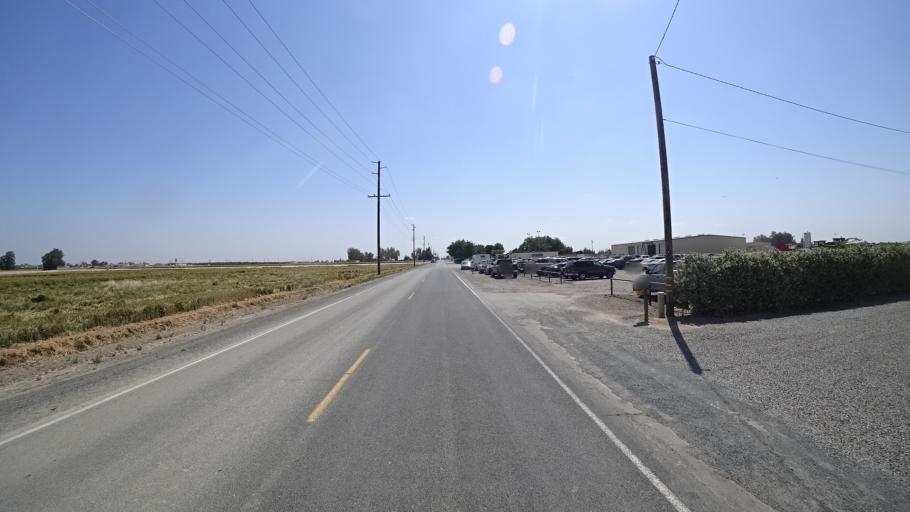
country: US
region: California
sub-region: Kings County
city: Home Garden
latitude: 36.3135
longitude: -119.6079
